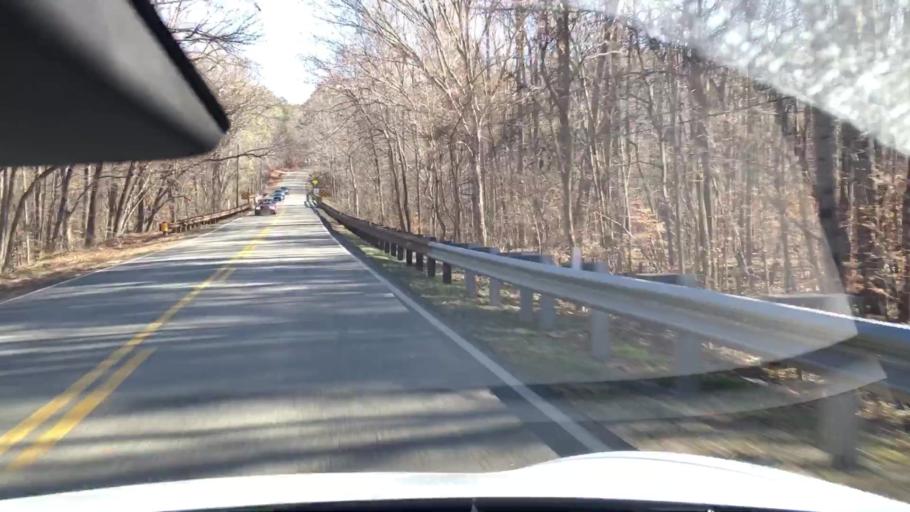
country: US
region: Virginia
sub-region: Henrico County
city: Short Pump
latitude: 37.5785
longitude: -77.7310
